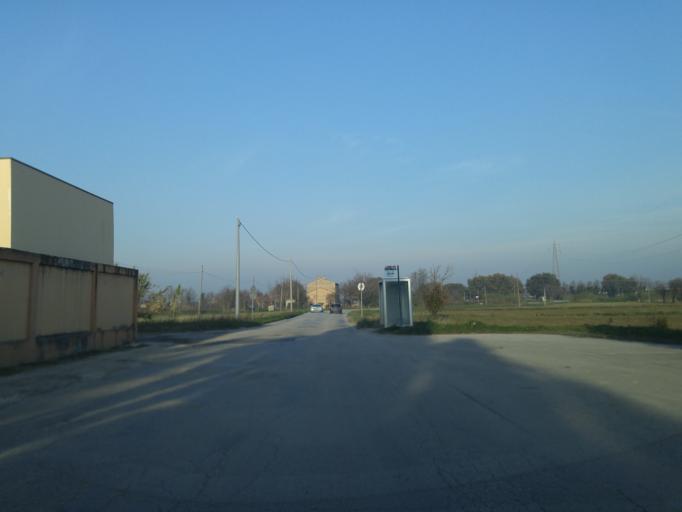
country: IT
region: The Marches
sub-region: Provincia di Pesaro e Urbino
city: Rosciano
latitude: 43.8125
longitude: 12.9936
